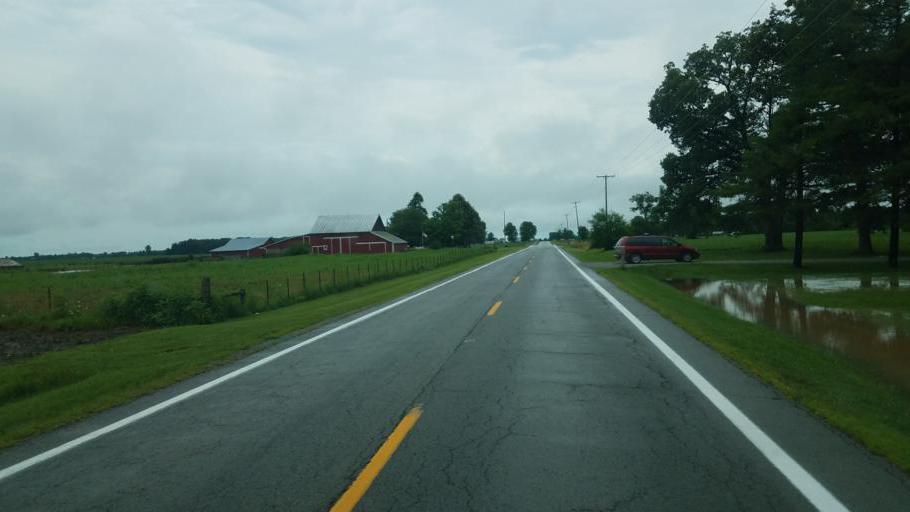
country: US
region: Ohio
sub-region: Union County
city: Richwood
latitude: 40.5075
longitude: -83.2697
